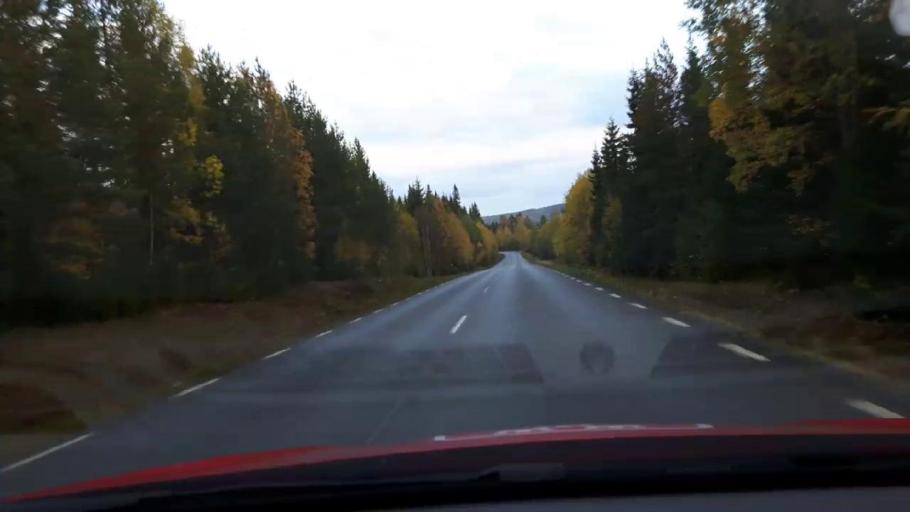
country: SE
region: Jaemtland
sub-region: OEstersunds Kommun
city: Lit
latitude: 63.3129
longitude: 14.6817
